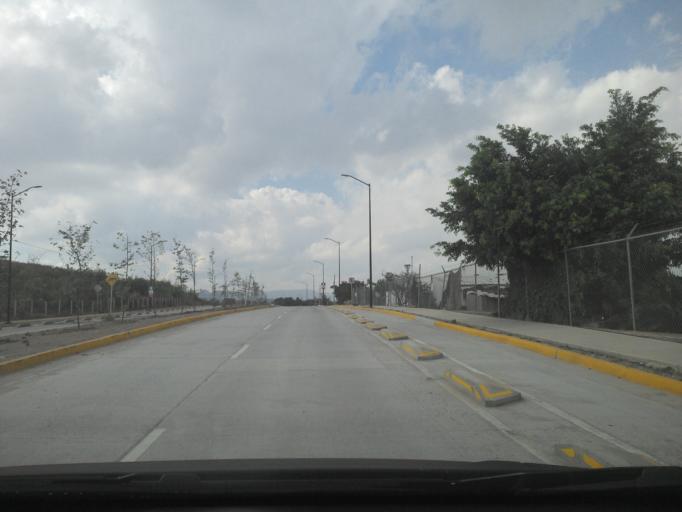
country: MX
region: Jalisco
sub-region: Tlajomulco de Zuniga
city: Altus Bosques
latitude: 20.6142
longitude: -103.3561
